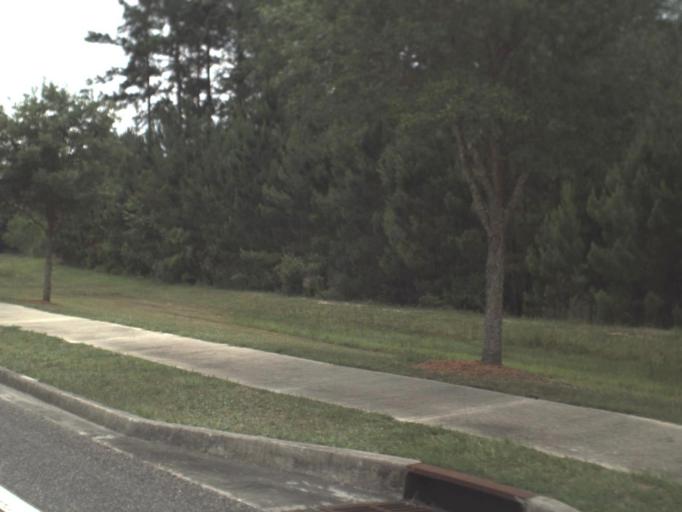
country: US
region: Florida
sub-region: Nassau County
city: Nassau Village-Ratliff
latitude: 30.4842
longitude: -81.6717
